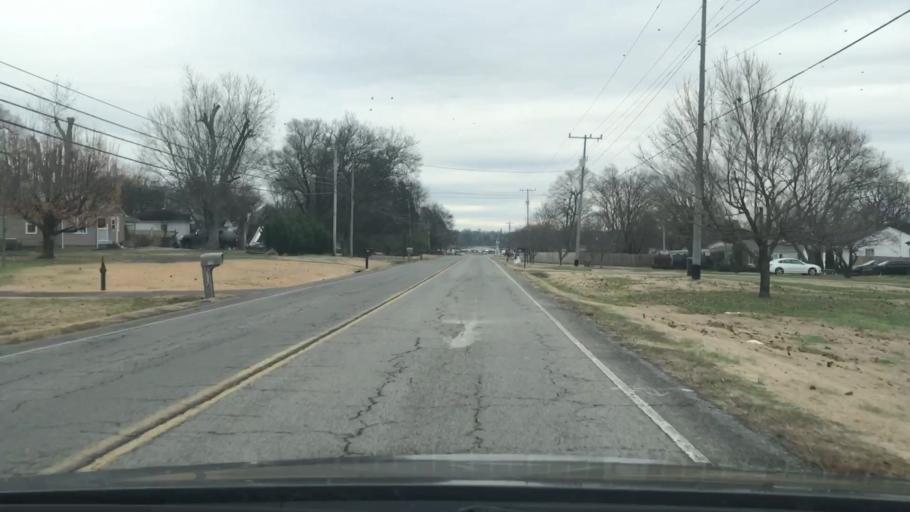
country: US
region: Tennessee
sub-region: Sumner County
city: Gallatin
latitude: 36.4201
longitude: -86.4574
